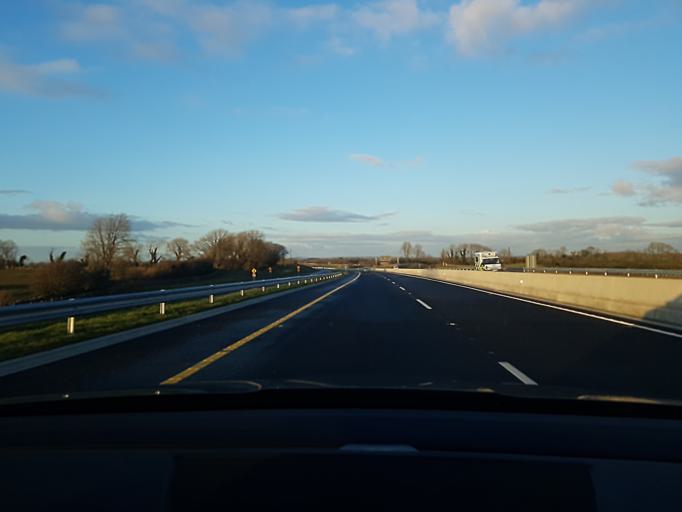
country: IE
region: Connaught
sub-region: County Galway
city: Athenry
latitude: 53.2997
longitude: -8.8057
